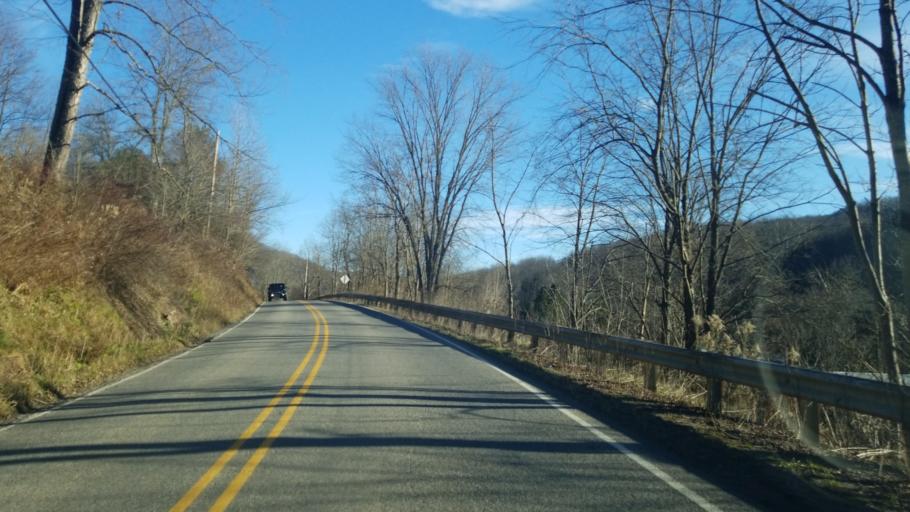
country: US
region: Pennsylvania
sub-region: Potter County
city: Coudersport
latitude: 41.6331
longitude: -78.1005
